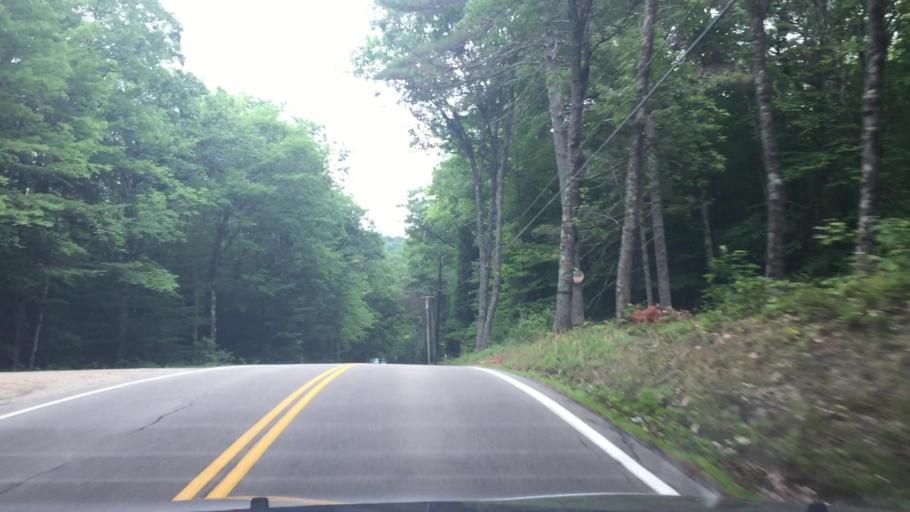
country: US
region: New Hampshire
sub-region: Carroll County
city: Madison
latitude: 43.8981
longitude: -71.0721
